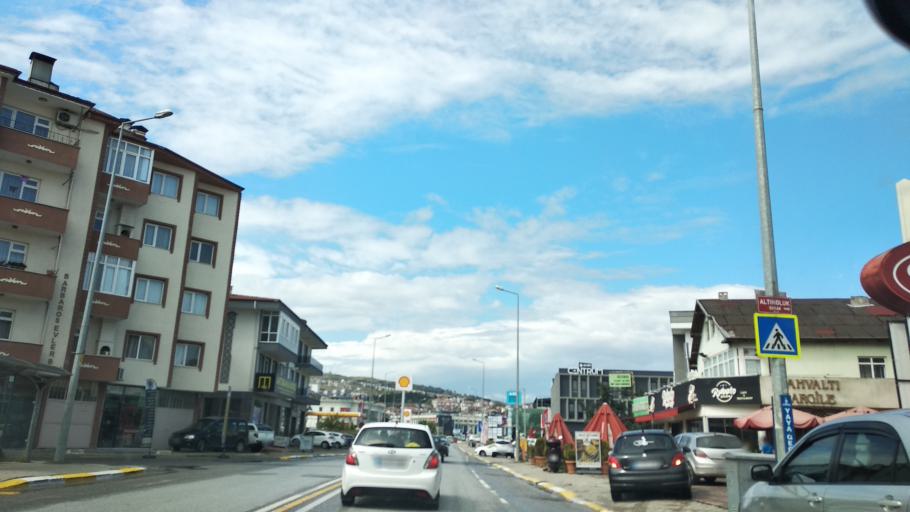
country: TR
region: Sakarya
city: Adapazari
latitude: 40.7584
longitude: 30.3674
